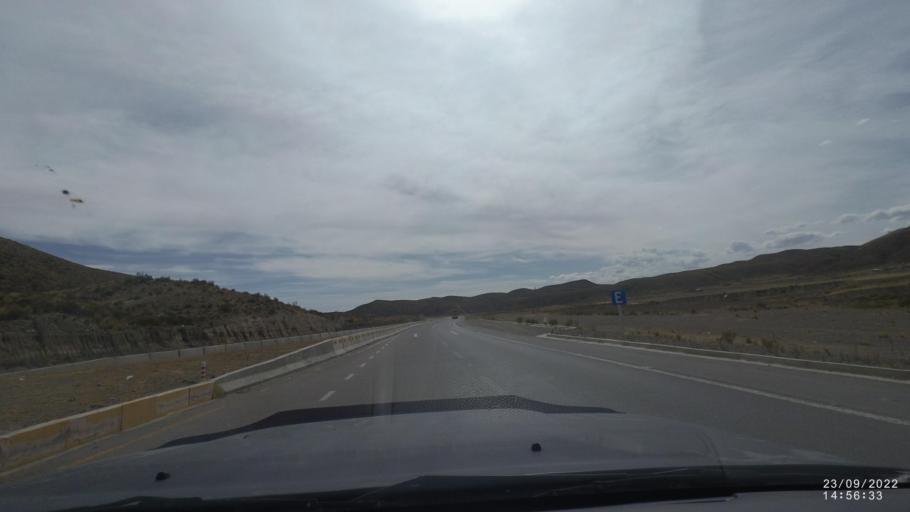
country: BO
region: La Paz
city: Colquiri
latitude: -17.6619
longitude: -67.0062
